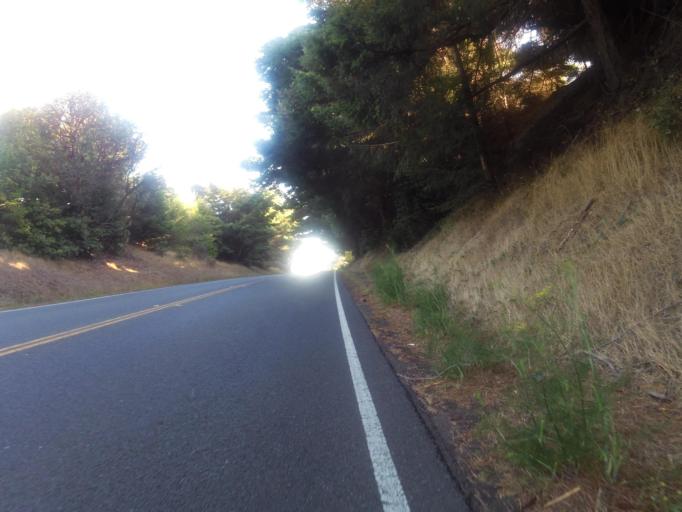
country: US
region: California
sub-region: Sonoma County
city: Sea Ranch
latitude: 38.7568
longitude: -123.5158
